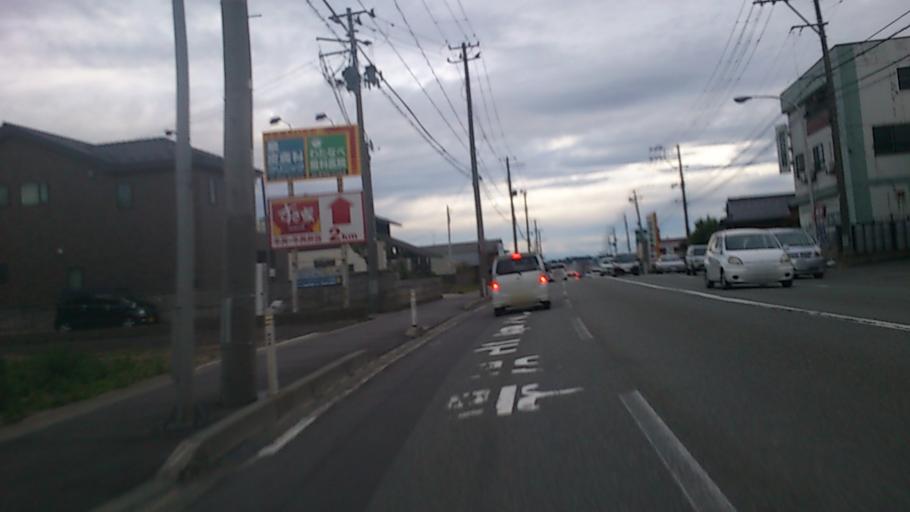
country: JP
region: Akita
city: Akita Shi
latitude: 39.7454
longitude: 140.0878
